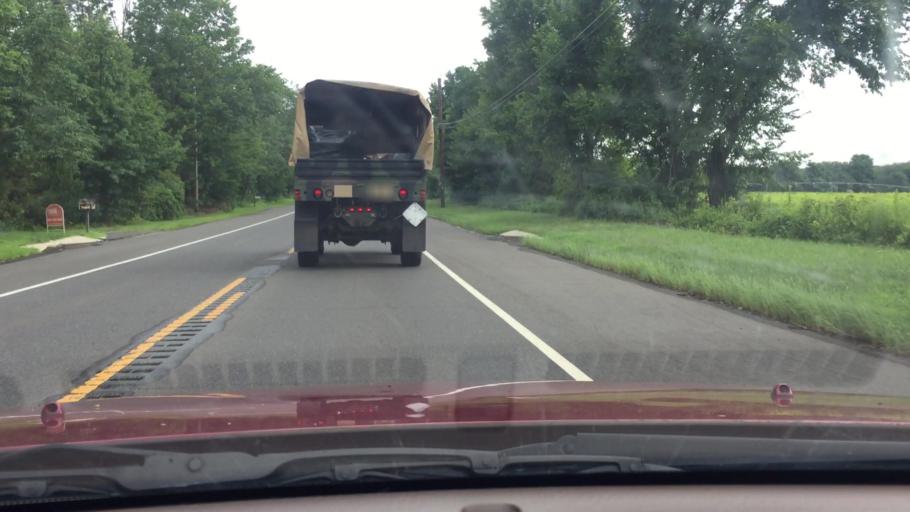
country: US
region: New Jersey
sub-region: Burlington County
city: Fort Dix
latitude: 40.0605
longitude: -74.6515
